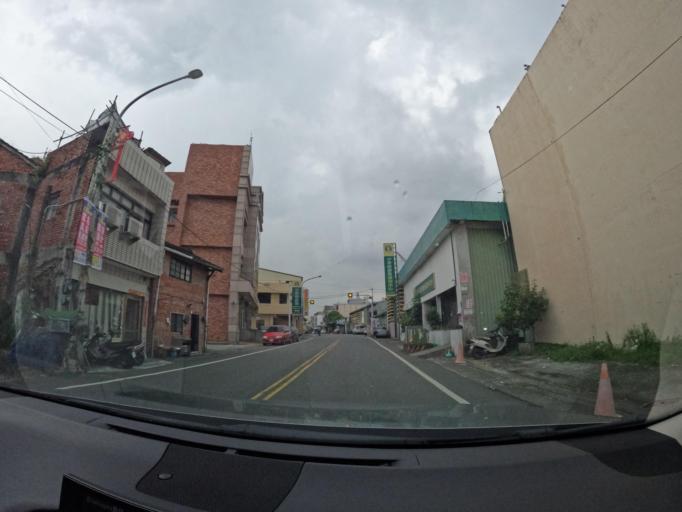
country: TW
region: Taiwan
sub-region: Nantou
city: Nantou
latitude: 23.8789
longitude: 120.7682
